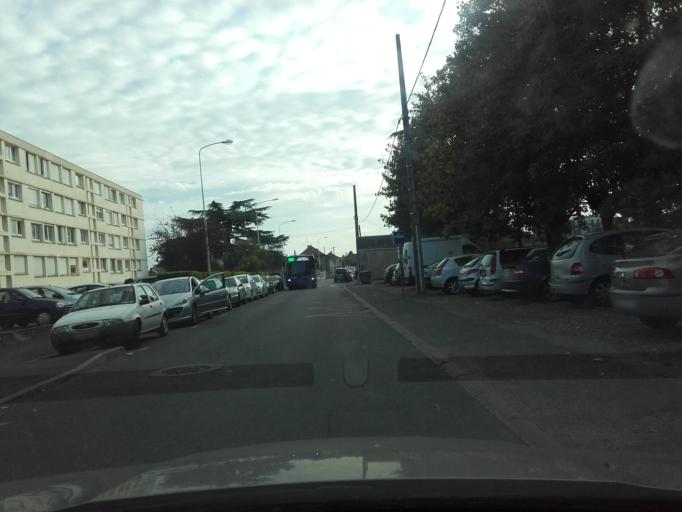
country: FR
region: Centre
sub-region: Departement d'Indre-et-Loire
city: Saint-Cyr-sur-Loire
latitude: 47.4134
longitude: 0.6966
